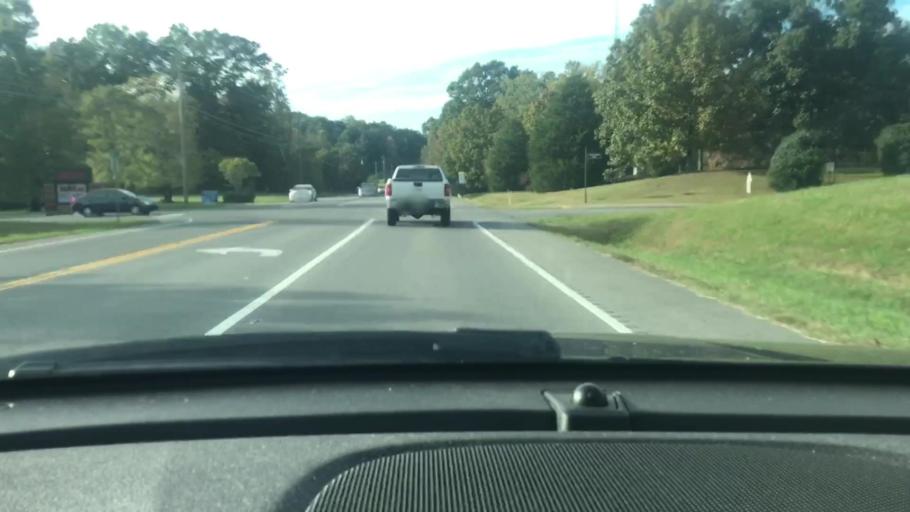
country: US
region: Tennessee
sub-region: Williamson County
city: Fairview
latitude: 35.9902
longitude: -87.1237
